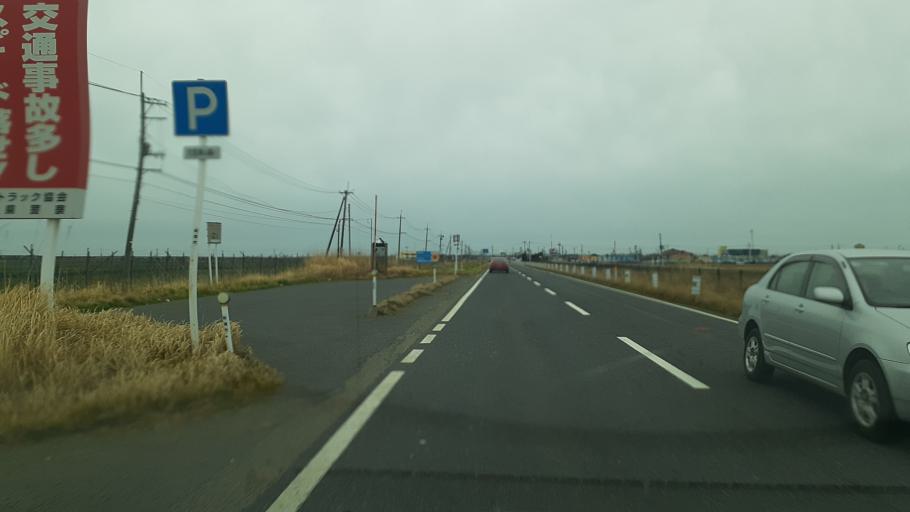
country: JP
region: Niigata
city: Niitsu-honcho
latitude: 37.8107
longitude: 139.1009
